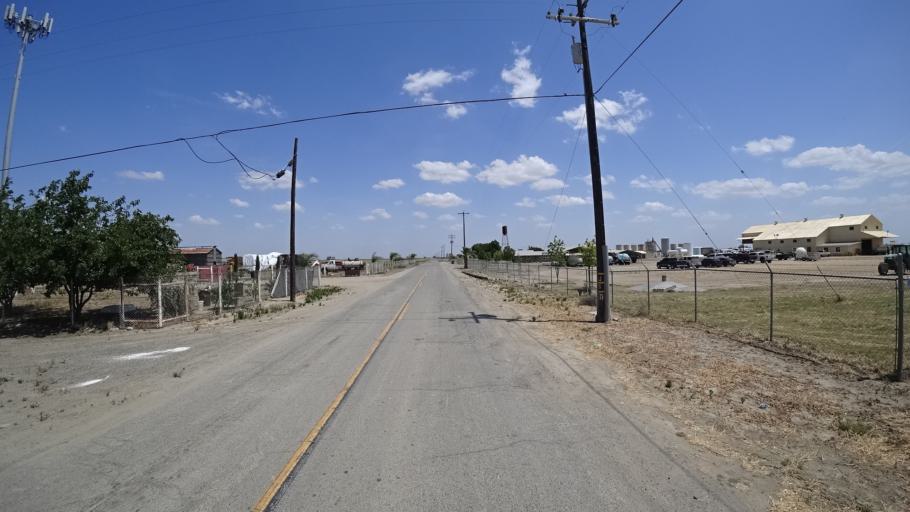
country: US
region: California
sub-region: Kings County
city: Stratford
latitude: 36.1820
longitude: -119.8249
